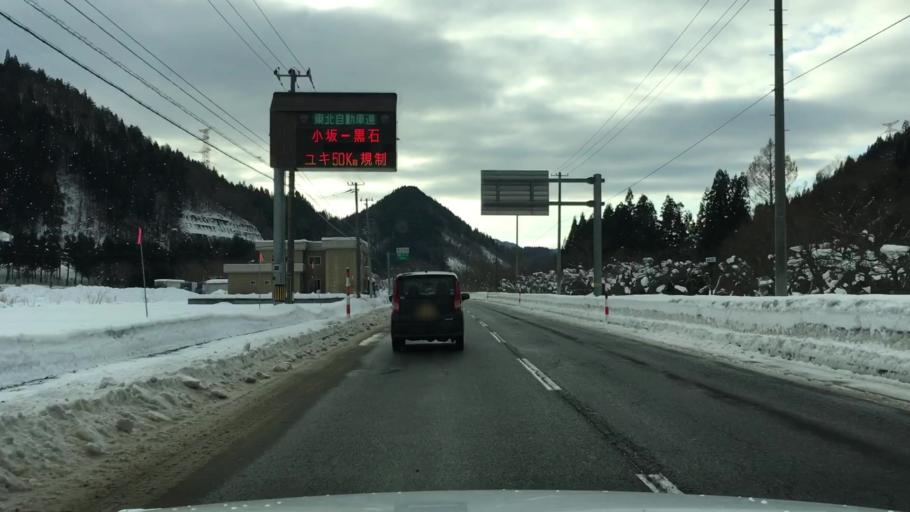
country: JP
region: Aomori
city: Kuroishi
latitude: 40.4660
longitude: 140.6338
